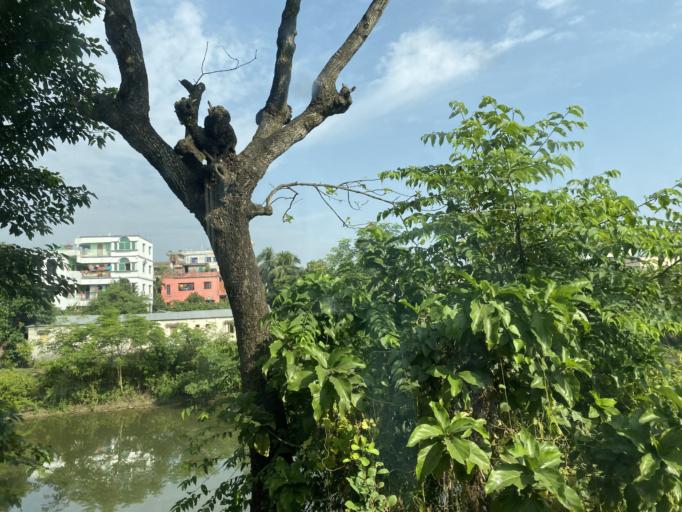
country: BD
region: Dhaka
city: Bhairab Bazar
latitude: 23.9679
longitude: 91.1136
